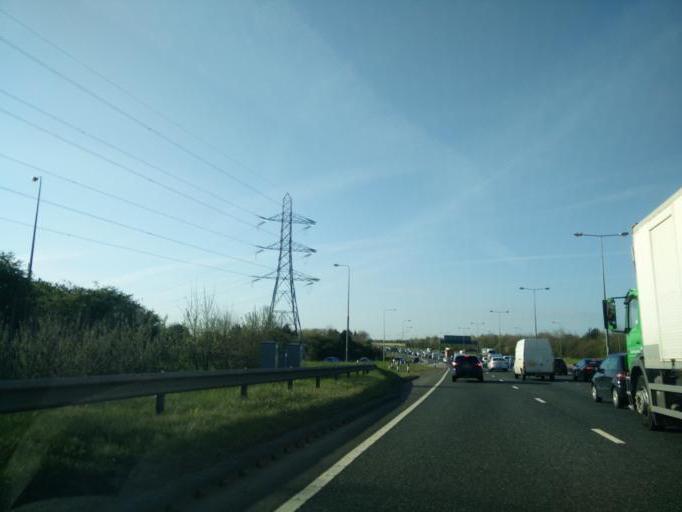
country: GB
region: England
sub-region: Stockton-on-Tees
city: Billingham
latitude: 54.5897
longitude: -1.3013
